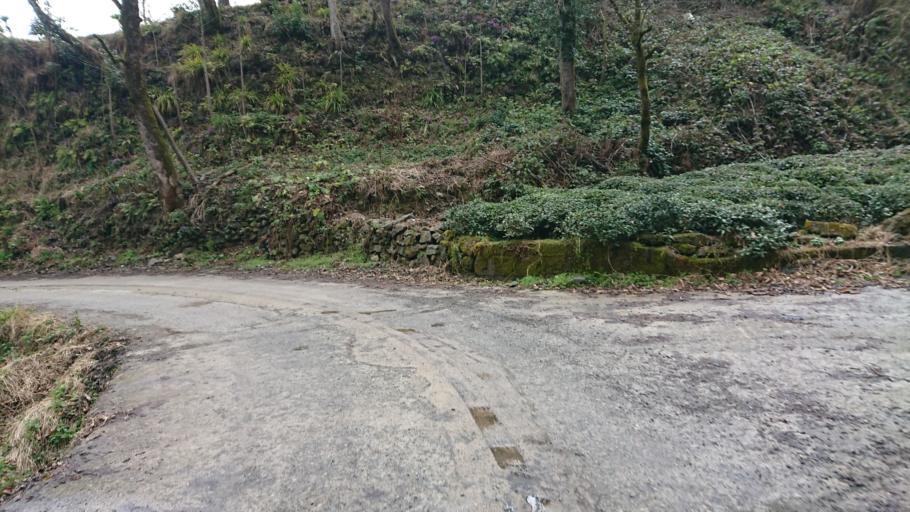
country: TR
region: Rize
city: Rize
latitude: 40.9809
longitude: 40.4966
